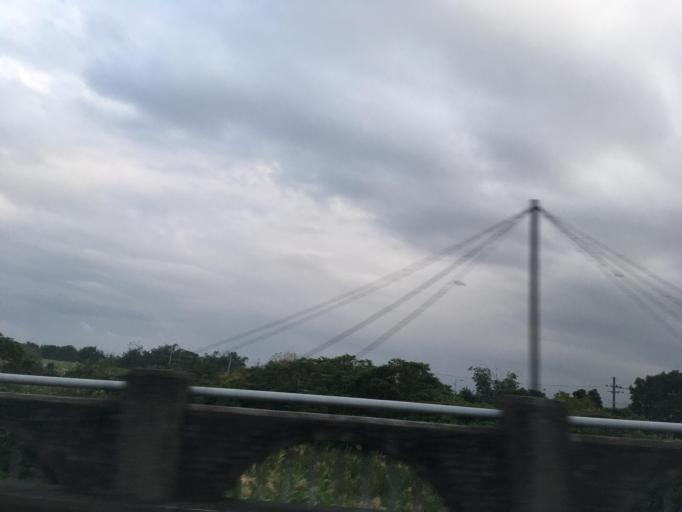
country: TW
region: Taiwan
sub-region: Yilan
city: Yilan
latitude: 24.7488
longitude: 121.7119
